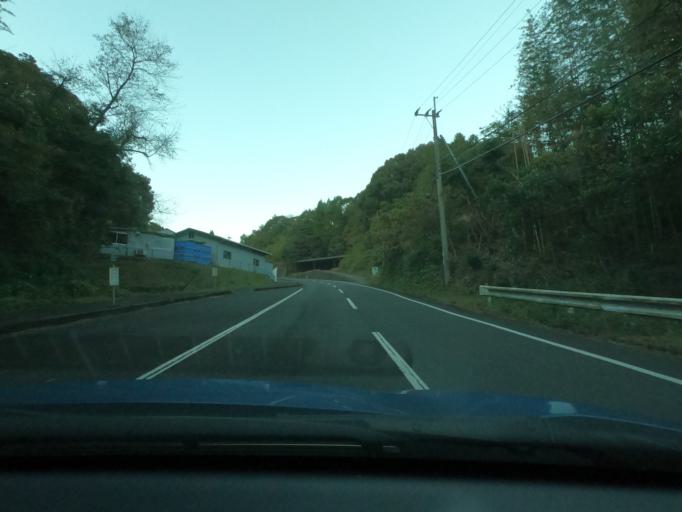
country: JP
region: Kagoshima
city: Satsumasendai
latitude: 31.8135
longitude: 130.4836
